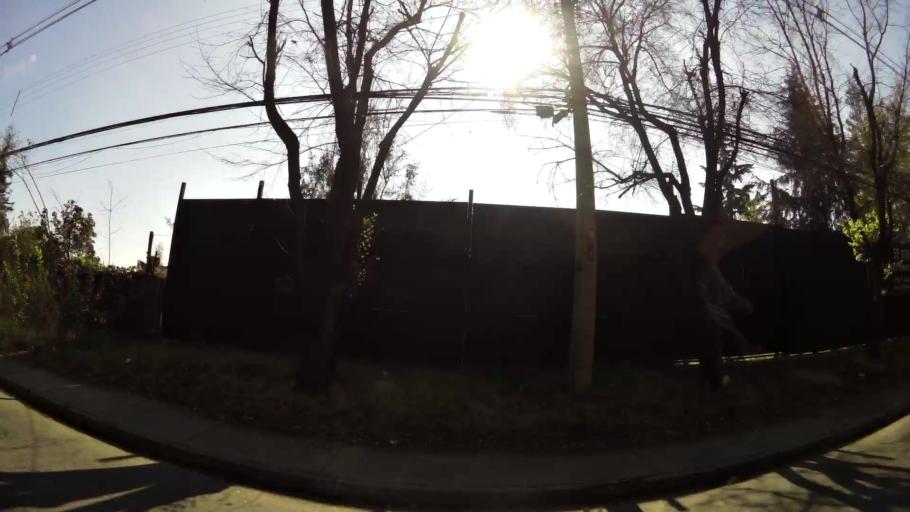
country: CL
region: Santiago Metropolitan
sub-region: Provincia de Santiago
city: Villa Presidente Frei, Nunoa, Santiago, Chile
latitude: -33.3895
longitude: -70.5201
